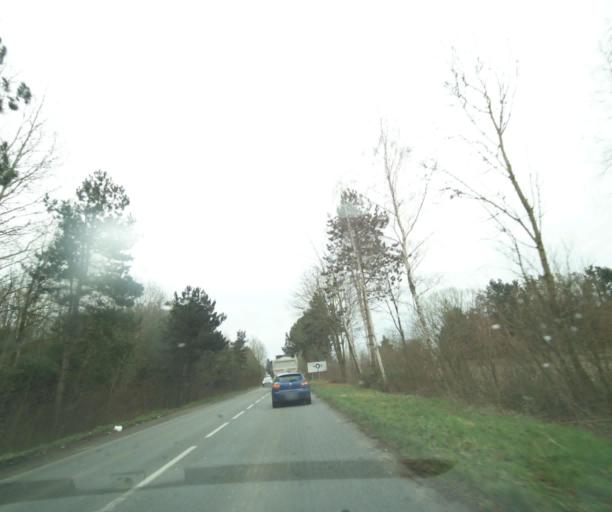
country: FR
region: Nord-Pas-de-Calais
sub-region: Departement du Nord
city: Quarouble
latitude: 50.3990
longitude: 3.6426
